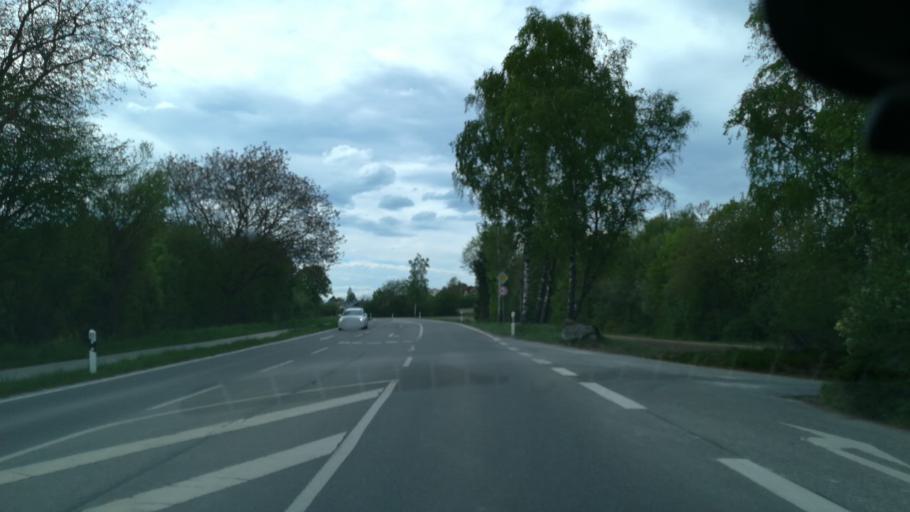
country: DE
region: Baden-Wuerttemberg
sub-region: Freiburg Region
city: Radolfzell am Bodensee
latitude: 47.7475
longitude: 8.9915
